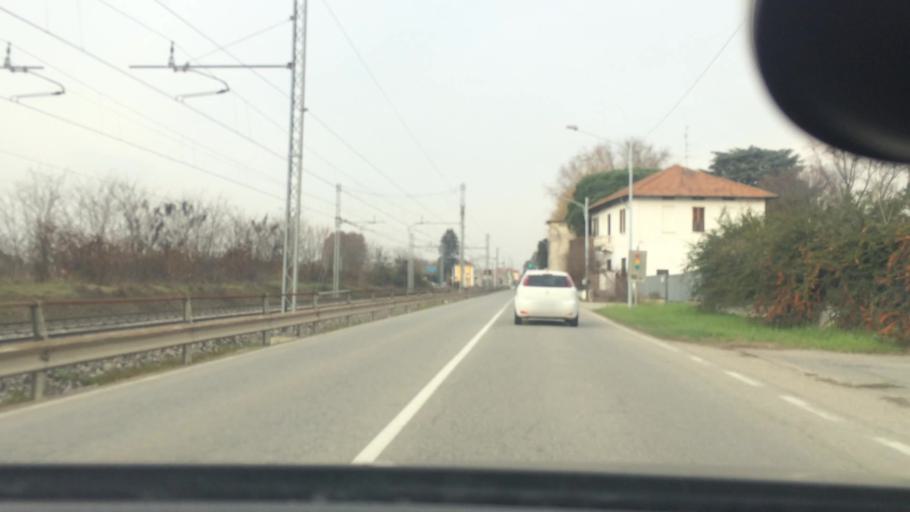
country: IT
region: Lombardy
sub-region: Provincia di Como
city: Manera
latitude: 45.6633
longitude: 9.0383
